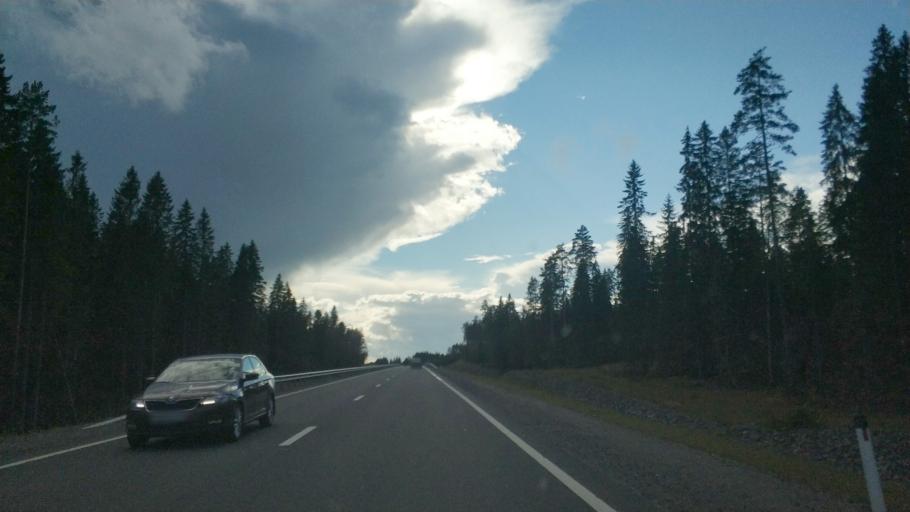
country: RU
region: Republic of Karelia
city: Lakhdenpokh'ya
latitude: 61.5059
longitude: 30.0518
